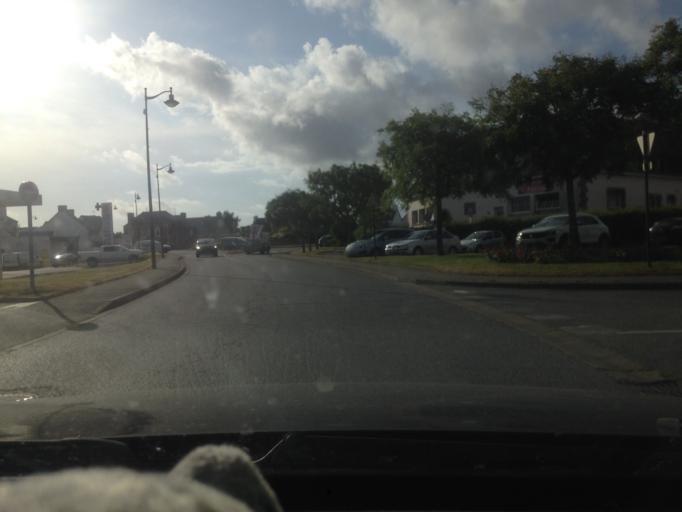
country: FR
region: Brittany
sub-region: Departement du Morbihan
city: Plouharnel
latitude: 47.5993
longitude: -3.1132
